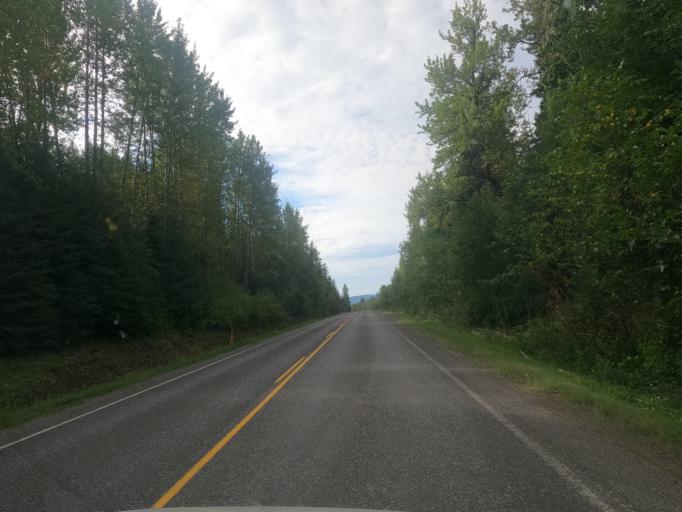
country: CA
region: British Columbia
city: Terrace
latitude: 55.3203
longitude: -128.0901
